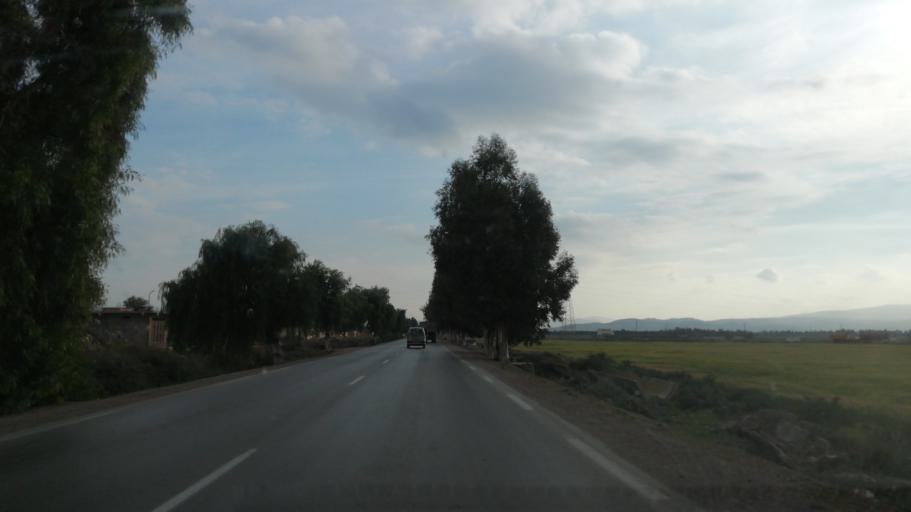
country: DZ
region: Mascara
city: Mascara
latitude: 35.6341
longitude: 0.0609
